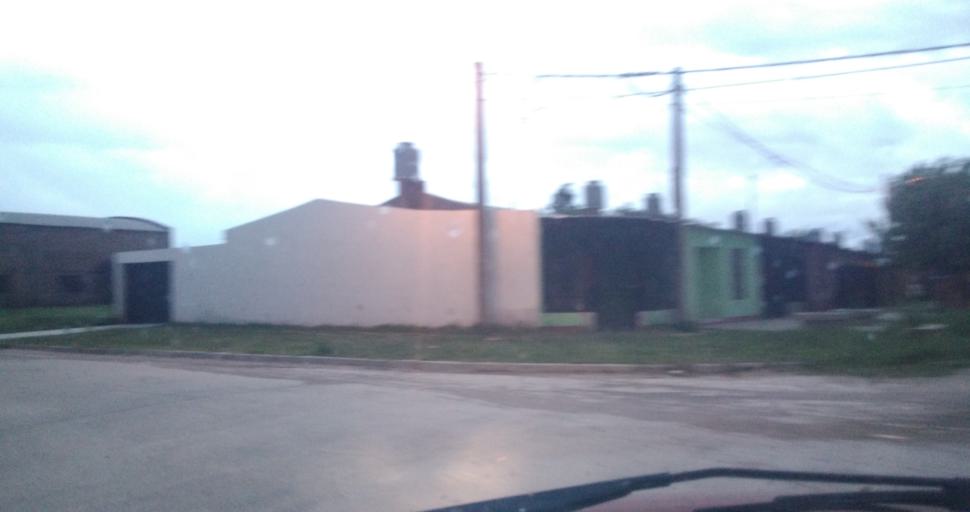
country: AR
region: Chaco
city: Fontana
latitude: -27.4176
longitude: -59.0456
